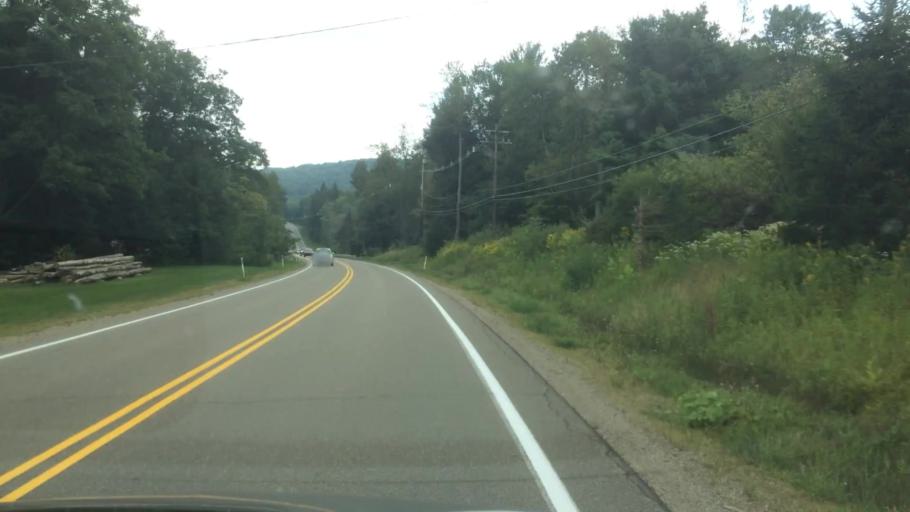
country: US
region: Pennsylvania
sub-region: McKean County
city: Bradford
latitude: 41.8933
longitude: -78.6066
